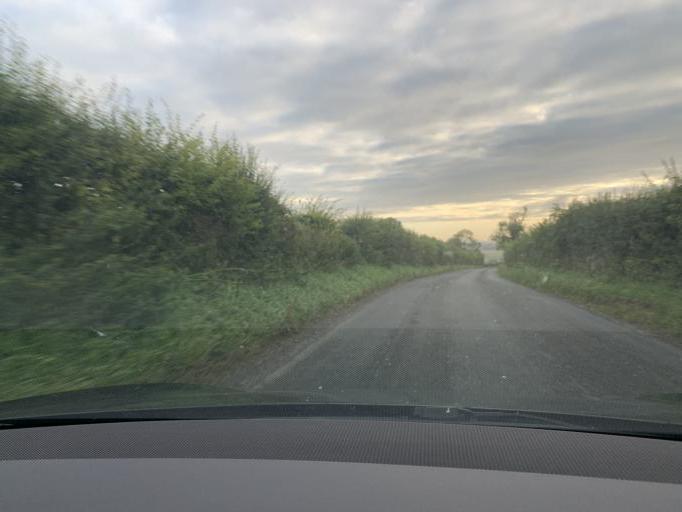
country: GB
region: England
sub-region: Wiltshire
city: Collingbourne Kingston
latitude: 51.3289
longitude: -1.6148
